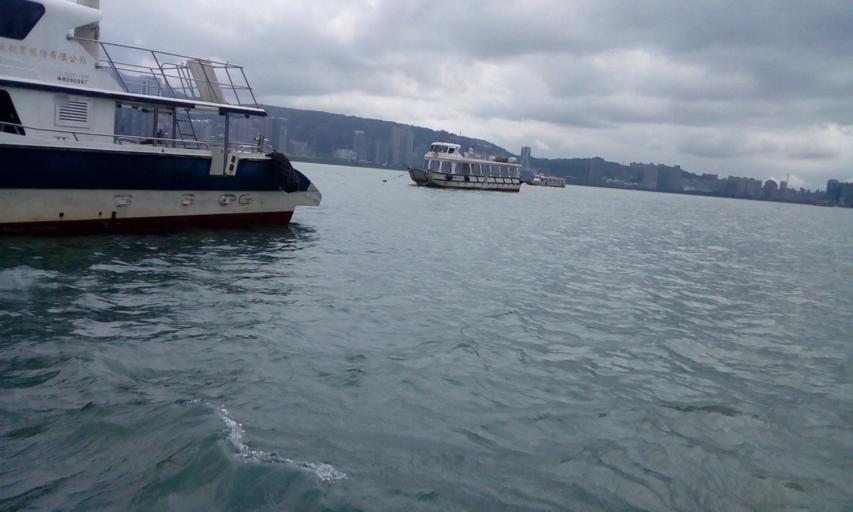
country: TW
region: Taipei
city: Taipei
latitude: 25.1610
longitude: 121.4362
